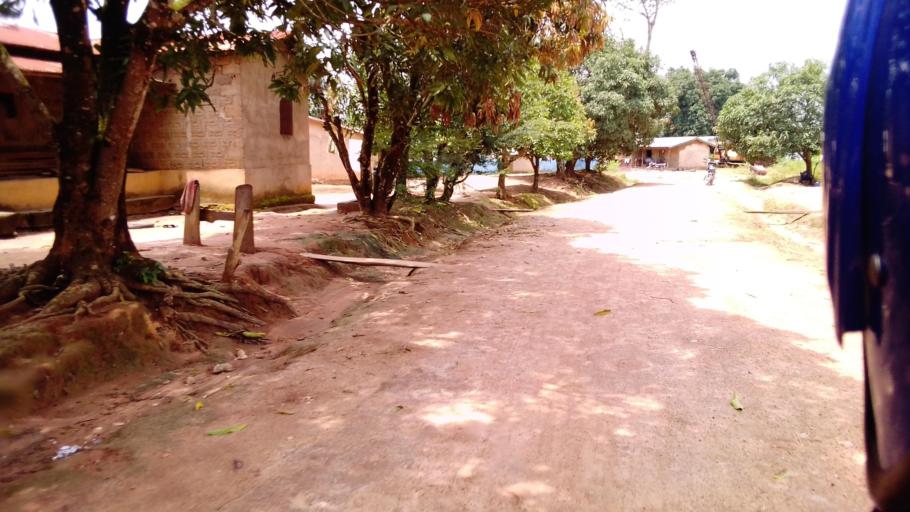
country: SL
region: Eastern Province
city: Koidu
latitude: 8.6664
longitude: -10.9451
